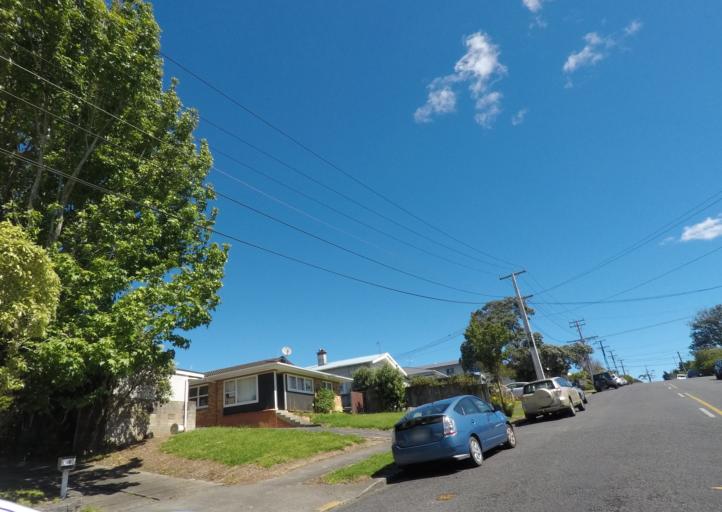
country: NZ
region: Auckland
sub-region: Auckland
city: Auckland
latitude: -36.8721
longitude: 174.7330
